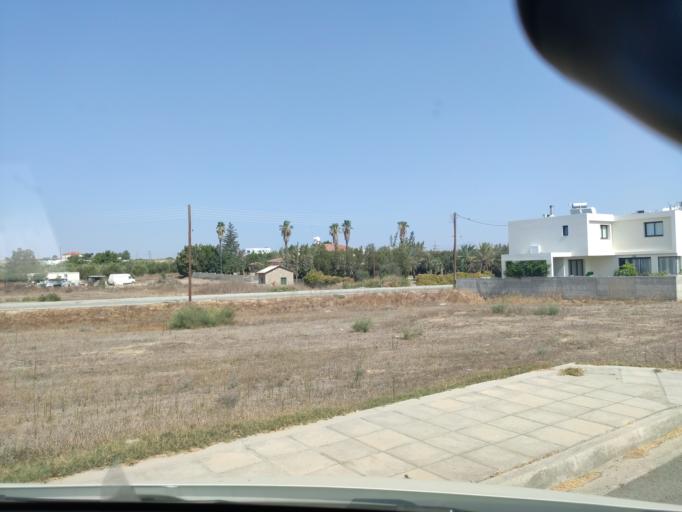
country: CY
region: Lefkosia
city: Geri
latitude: 35.1161
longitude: 33.4160
